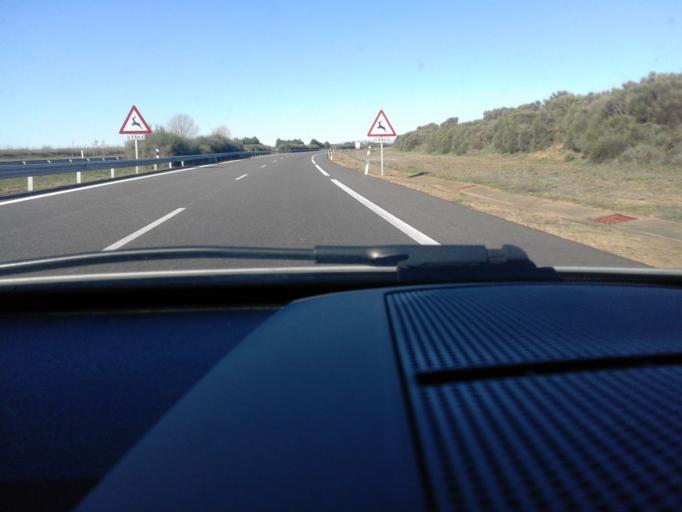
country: ES
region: Castille and Leon
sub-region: Provincia de Leon
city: Vega de Infanzones
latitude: 42.4651
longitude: -5.5428
